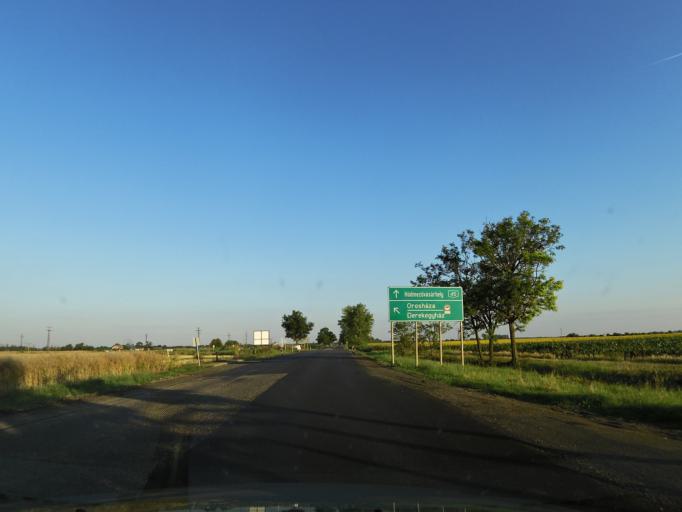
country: HU
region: Csongrad
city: Szentes
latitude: 46.5968
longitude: 20.2945
